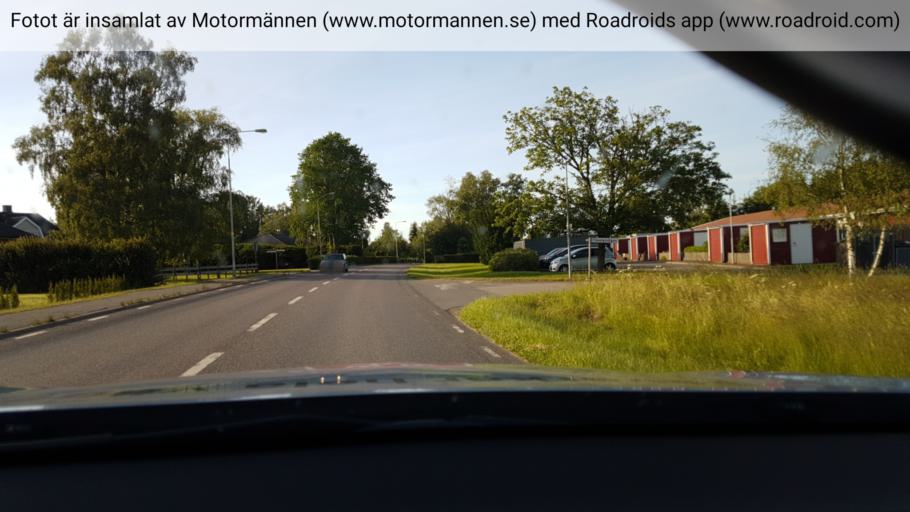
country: SE
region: Vaestra Goetaland
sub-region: Falkopings Kommun
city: Falkoeping
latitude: 58.0809
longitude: 13.5163
